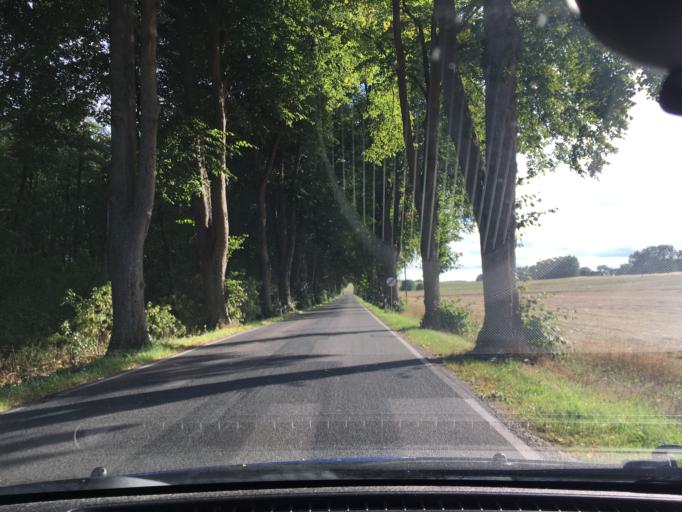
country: DE
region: Lower Saxony
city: Stelle
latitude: 53.3422
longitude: 10.0853
